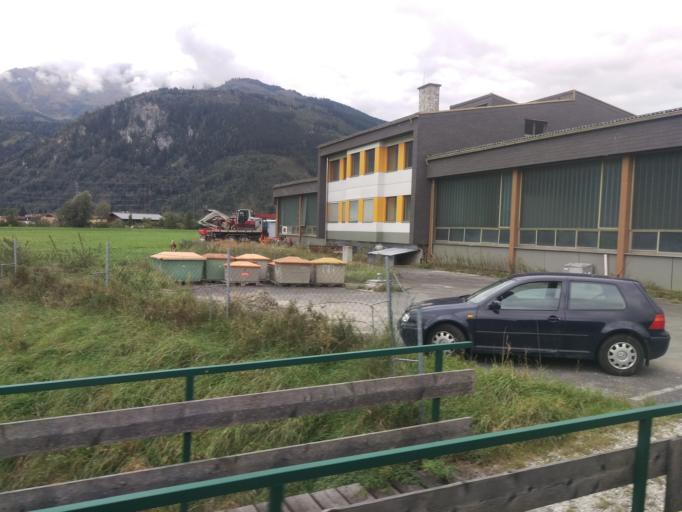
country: AT
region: Salzburg
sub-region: Politischer Bezirk Zell am See
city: Uttendorf
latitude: 47.2815
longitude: 12.5730
